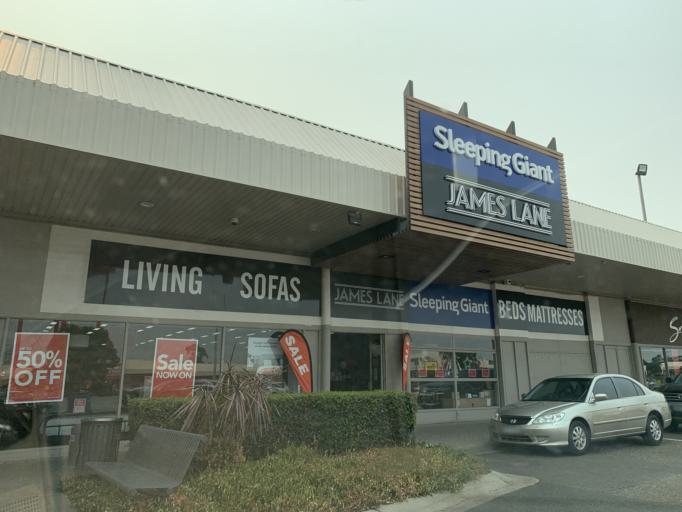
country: AU
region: New South Wales
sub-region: Holroyd
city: Girraween
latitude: -33.8018
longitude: 150.9187
